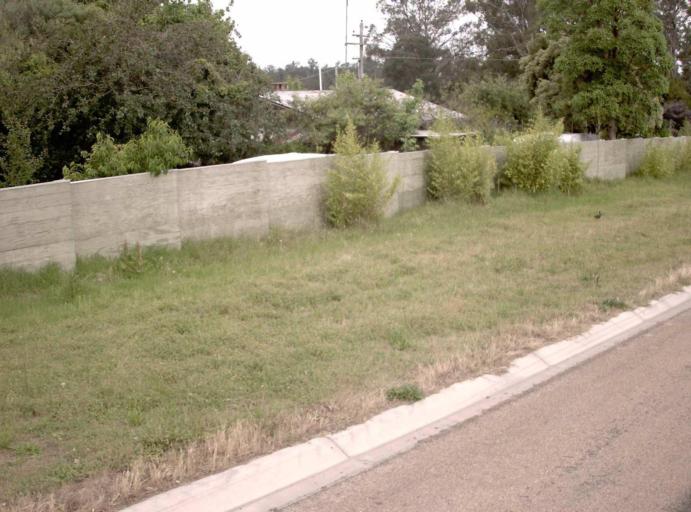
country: AU
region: Victoria
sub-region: East Gippsland
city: Lakes Entrance
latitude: -37.7295
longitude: 148.0892
